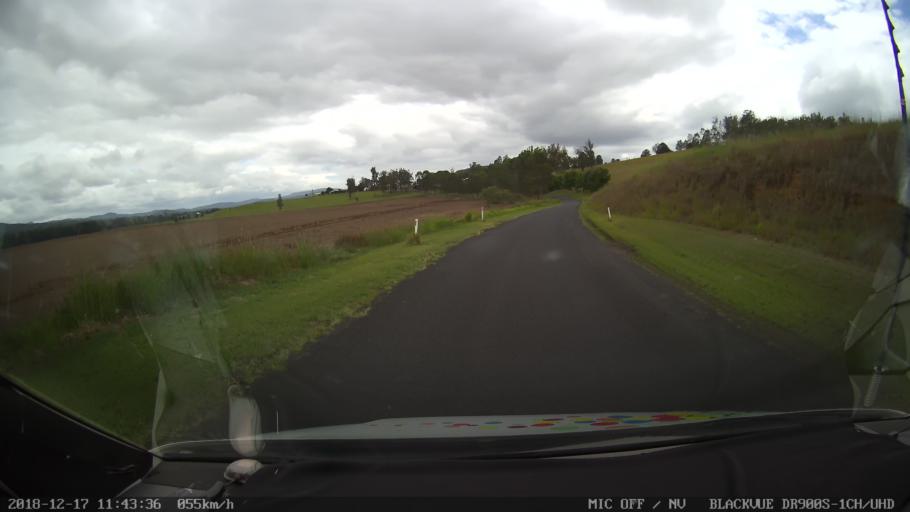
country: AU
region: New South Wales
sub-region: Kyogle
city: Kyogle
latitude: -28.6586
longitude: 152.5932
